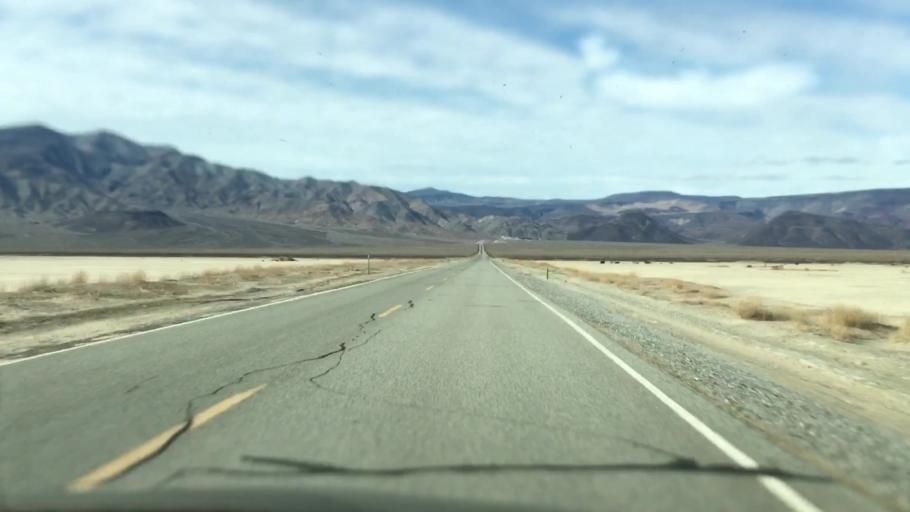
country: US
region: California
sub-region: San Bernardino County
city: Searles Valley
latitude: 36.3413
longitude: -117.4017
